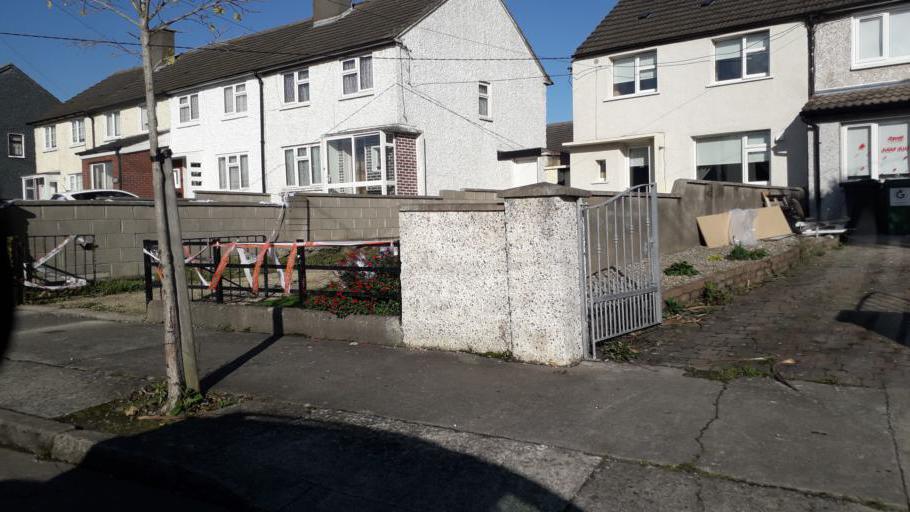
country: IE
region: Leinster
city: Raheny
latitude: 53.3853
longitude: -6.1846
